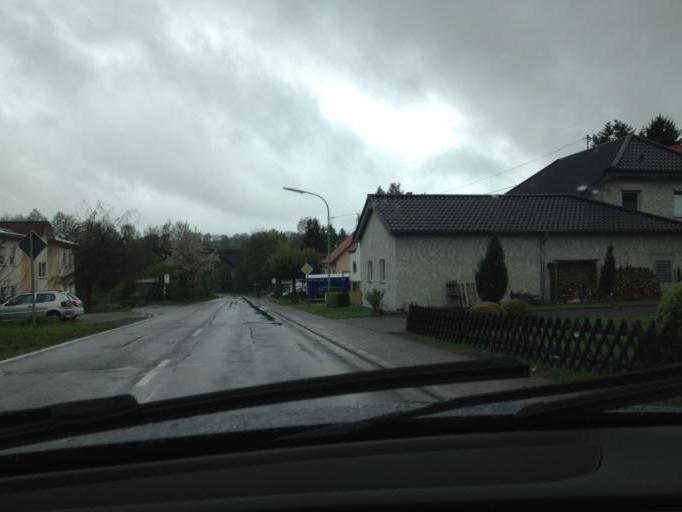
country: DE
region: Rheinland-Pfalz
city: Herchweiler
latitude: 49.5092
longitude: 7.2716
